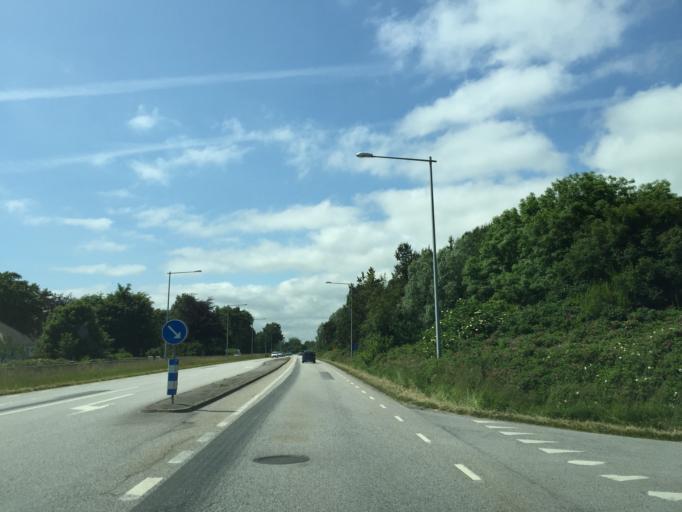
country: SE
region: Skane
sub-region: Ystads Kommun
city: Kopingebro
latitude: 55.4337
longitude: 13.9394
